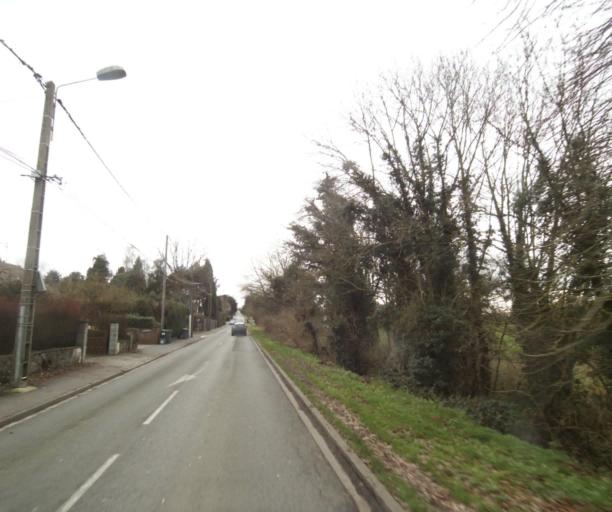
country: FR
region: Nord-Pas-de-Calais
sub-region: Departement du Nord
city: Valenciennes
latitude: 50.3622
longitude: 3.5429
